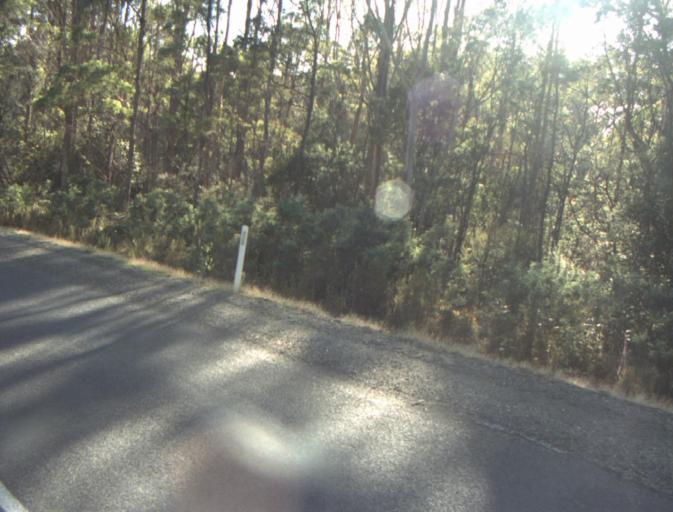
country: AU
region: Tasmania
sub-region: Launceston
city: Mayfield
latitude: -41.3354
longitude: 147.1780
